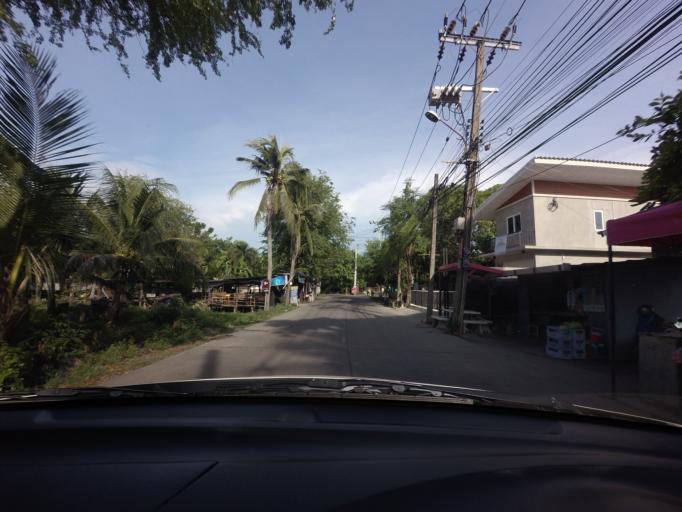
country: TH
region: Bangkok
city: Yan Nawa
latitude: 13.6821
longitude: 100.5636
